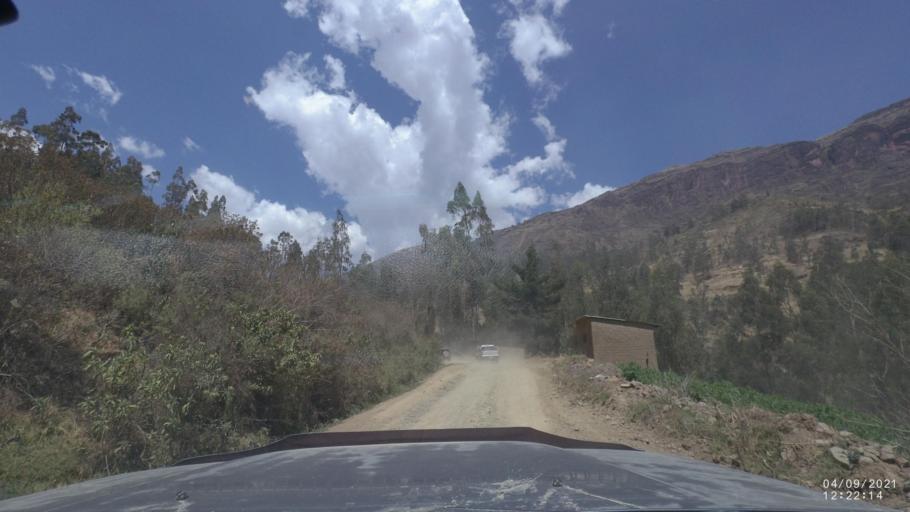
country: BO
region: Cochabamba
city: Colchani
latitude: -17.2381
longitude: -66.5260
